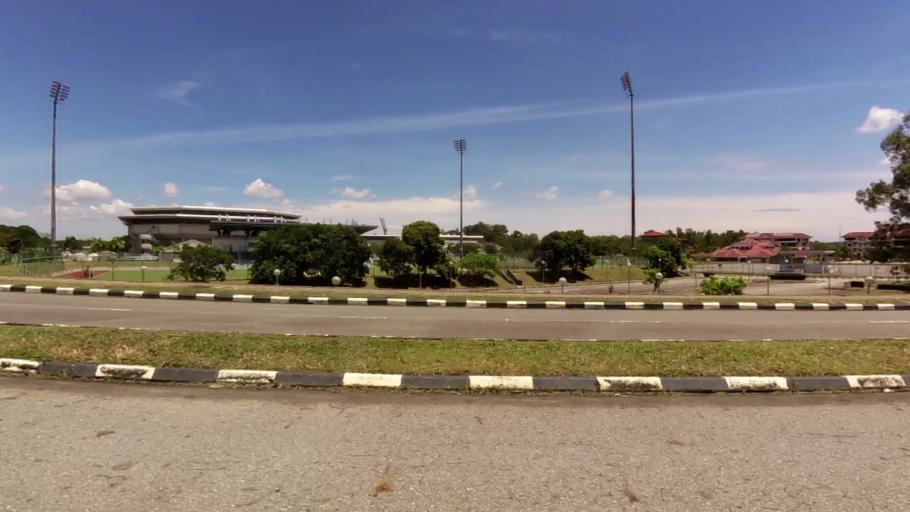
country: BN
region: Brunei and Muara
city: Bandar Seri Begawan
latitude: 4.9275
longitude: 114.9518
